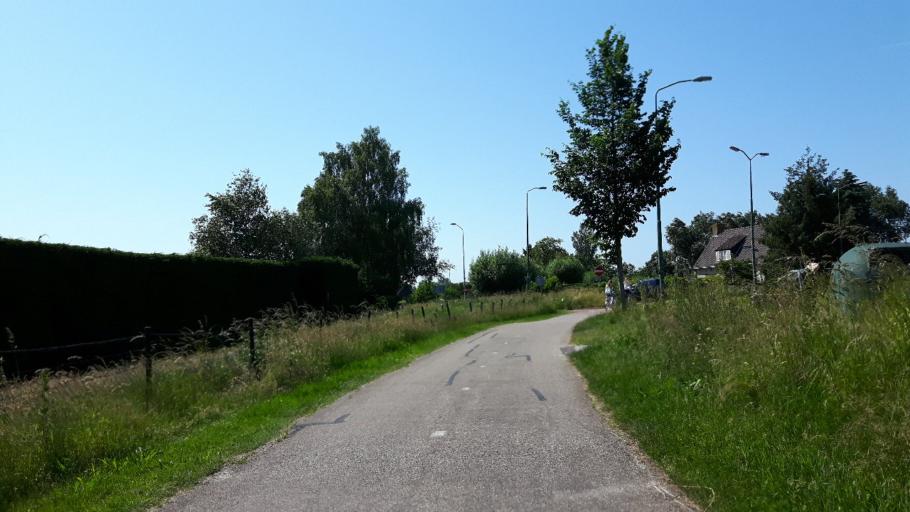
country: NL
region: North Holland
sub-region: Gemeente Wijdemeren
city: Kortenhoef
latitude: 52.2549
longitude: 5.0951
